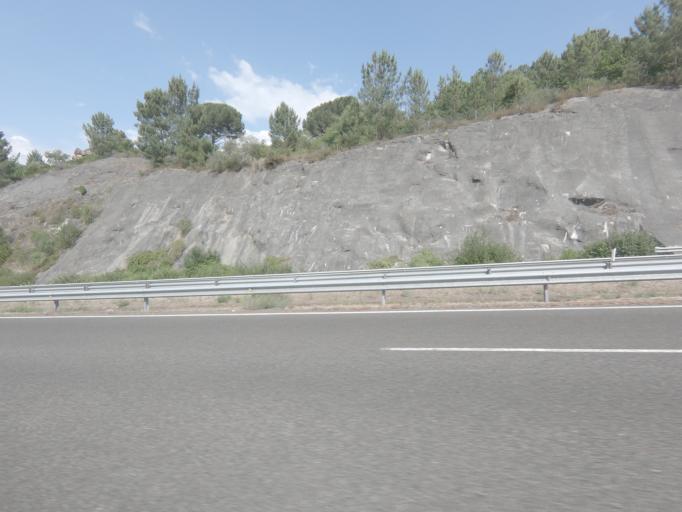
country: ES
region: Galicia
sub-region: Provincia de Ourense
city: Ourense
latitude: 42.2970
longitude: -7.8773
